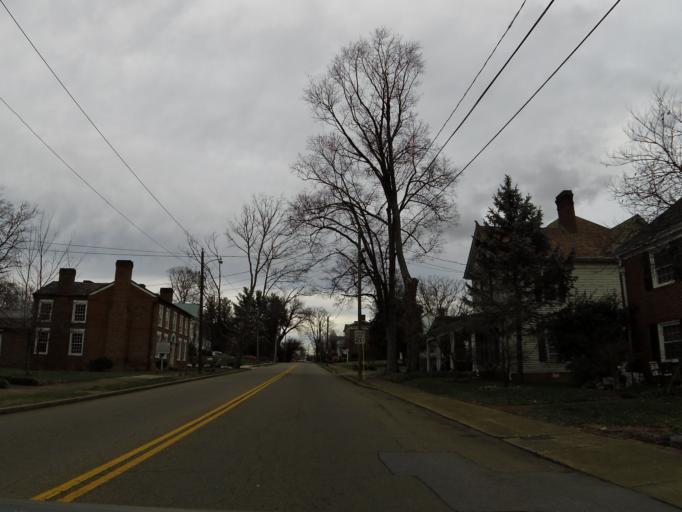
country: US
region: Tennessee
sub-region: Greene County
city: Greeneville
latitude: 36.1673
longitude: -82.8286
